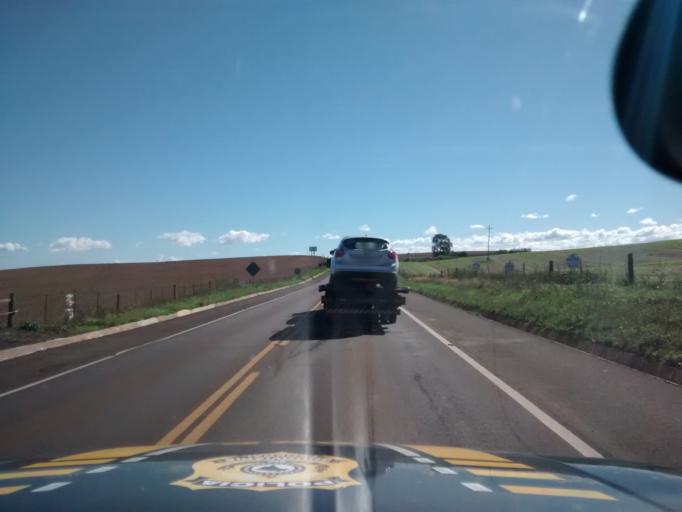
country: BR
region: Rio Grande do Sul
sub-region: Vacaria
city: Vacaria
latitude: -28.3727
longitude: -51.0856
